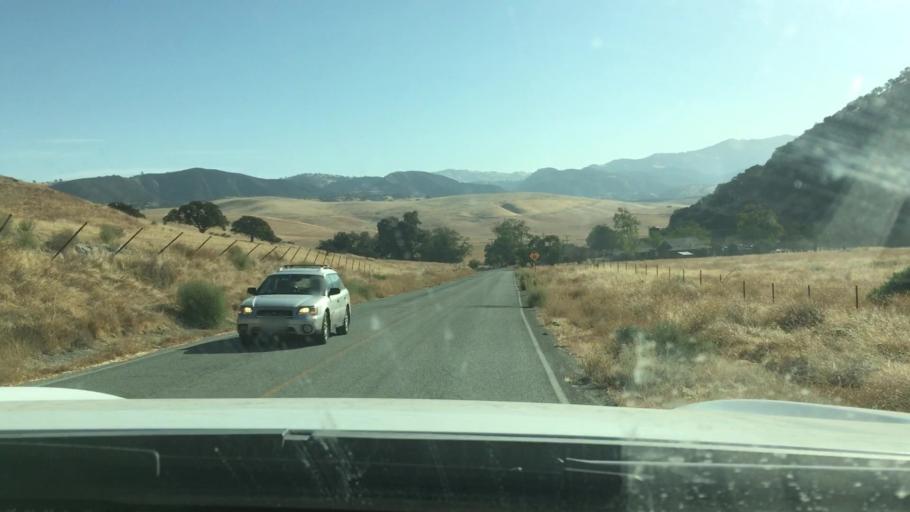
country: US
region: California
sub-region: Monterey County
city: King City
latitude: 36.3803
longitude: -121.0052
